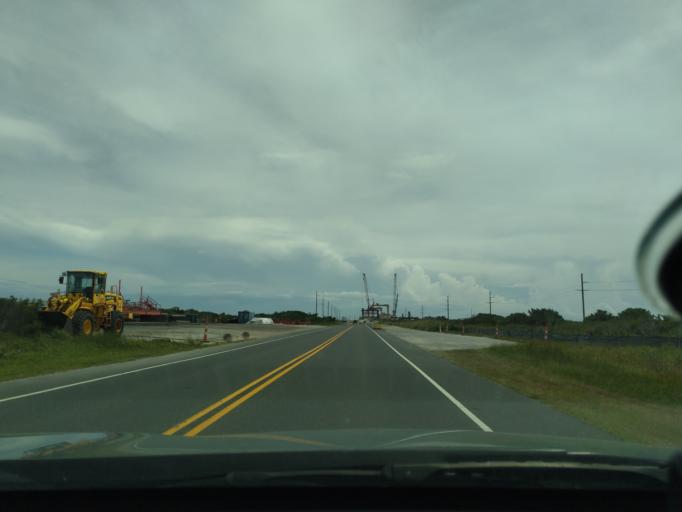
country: US
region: North Carolina
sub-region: Dare County
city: Wanchese
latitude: 35.6364
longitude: -75.4725
